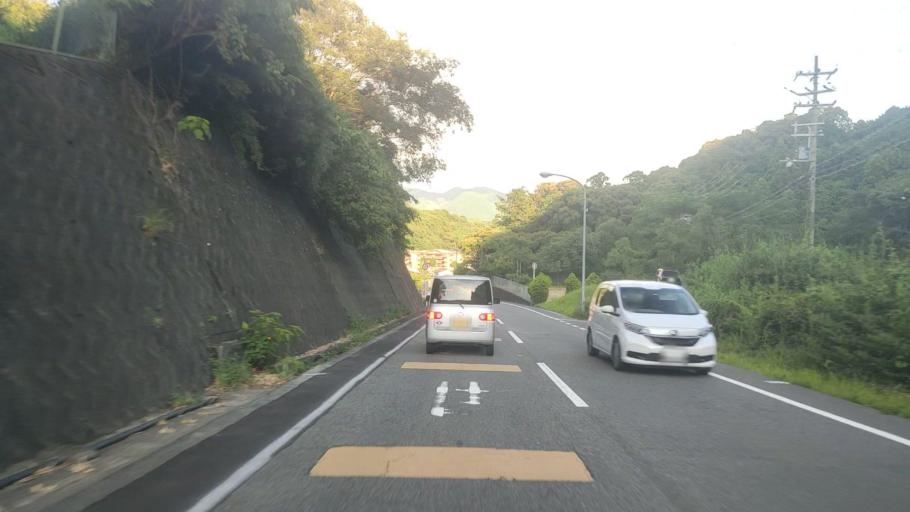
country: JP
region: Wakayama
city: Tanabe
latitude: 33.7270
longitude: 135.4392
